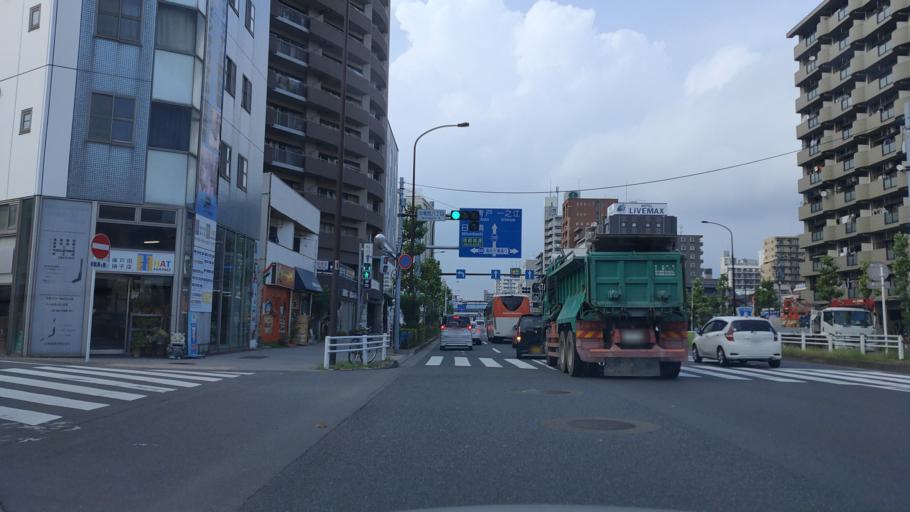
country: JP
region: Tokyo
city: Urayasu
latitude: 35.6590
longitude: 139.8727
